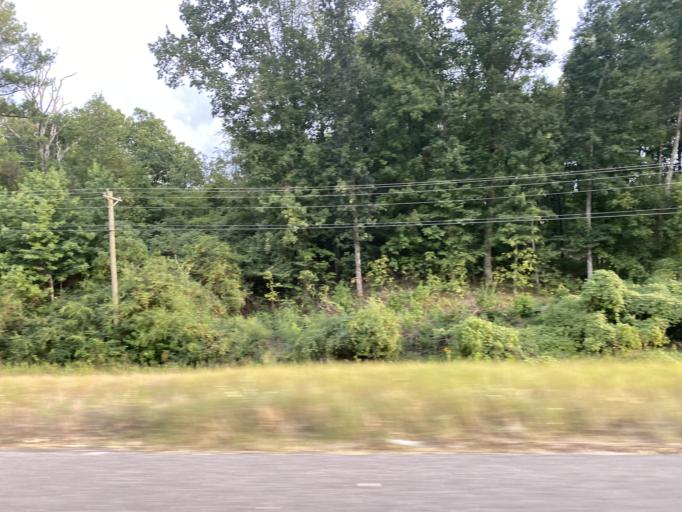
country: US
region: Alabama
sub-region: Franklin County
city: Red Bay
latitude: 34.4492
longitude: -88.0704
